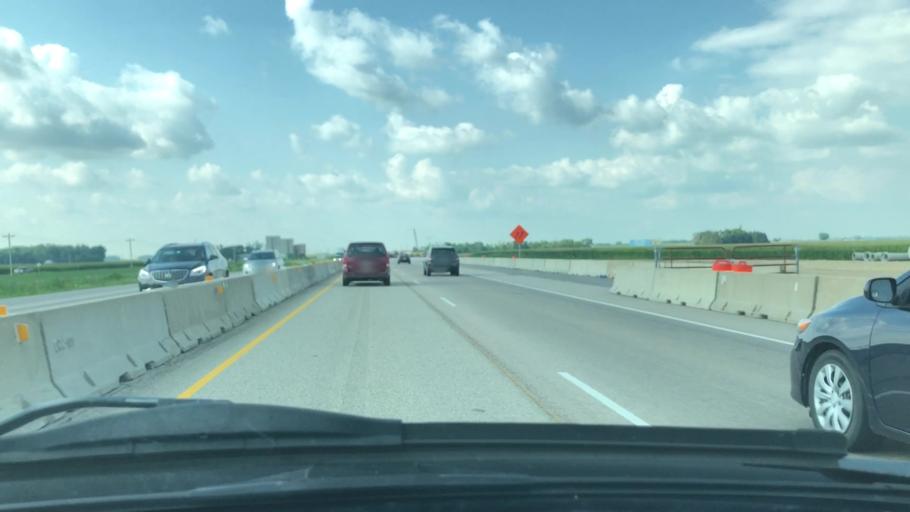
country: US
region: Wisconsin
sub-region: Rock County
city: Beloit
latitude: 42.5763
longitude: -88.9816
